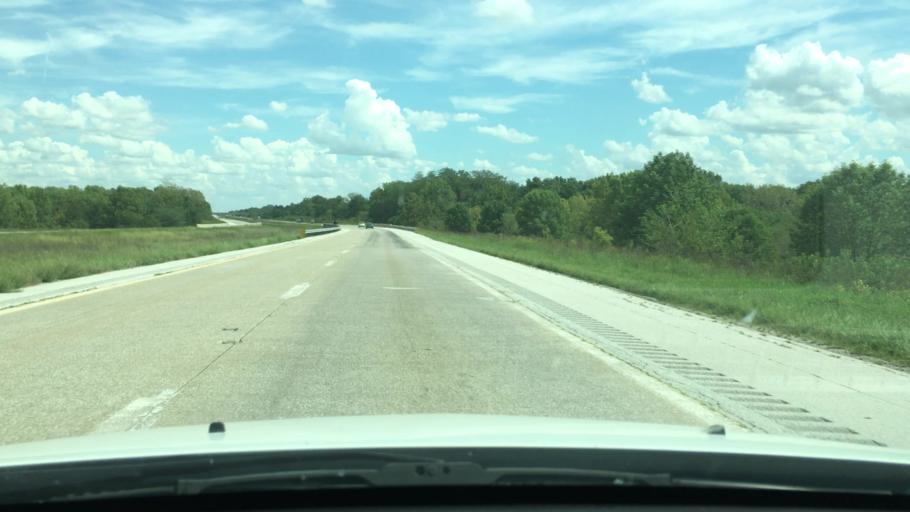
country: US
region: Illinois
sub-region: Scott County
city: Winchester
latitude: 39.6815
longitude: -90.5232
